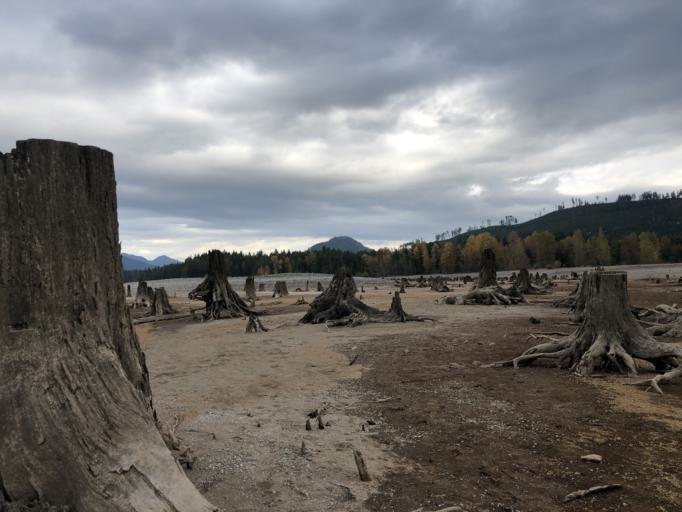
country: US
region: Washington
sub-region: Mason County
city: Shelton
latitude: 47.4608
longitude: -123.2275
